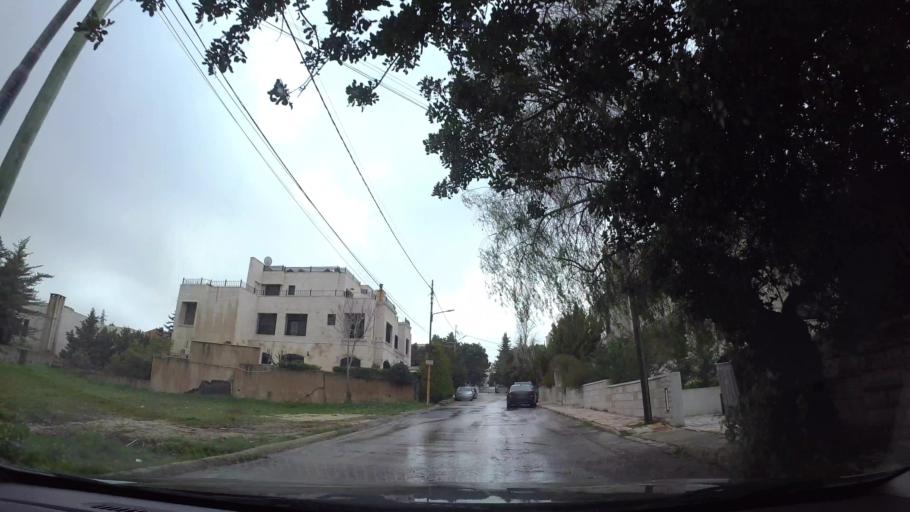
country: JO
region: Amman
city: Al Bunayyat ash Shamaliyah
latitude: 31.9482
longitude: 35.8878
